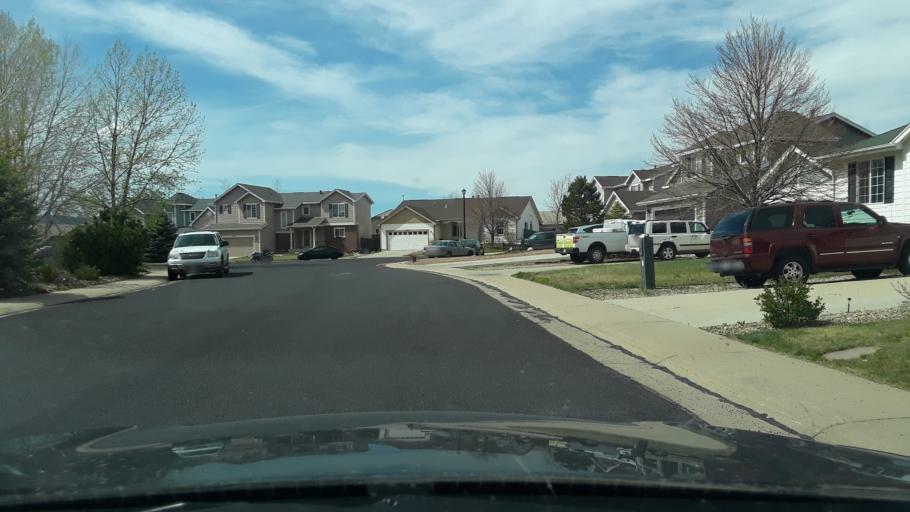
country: US
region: Colorado
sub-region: El Paso County
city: Monument
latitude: 39.0813
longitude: -104.8664
